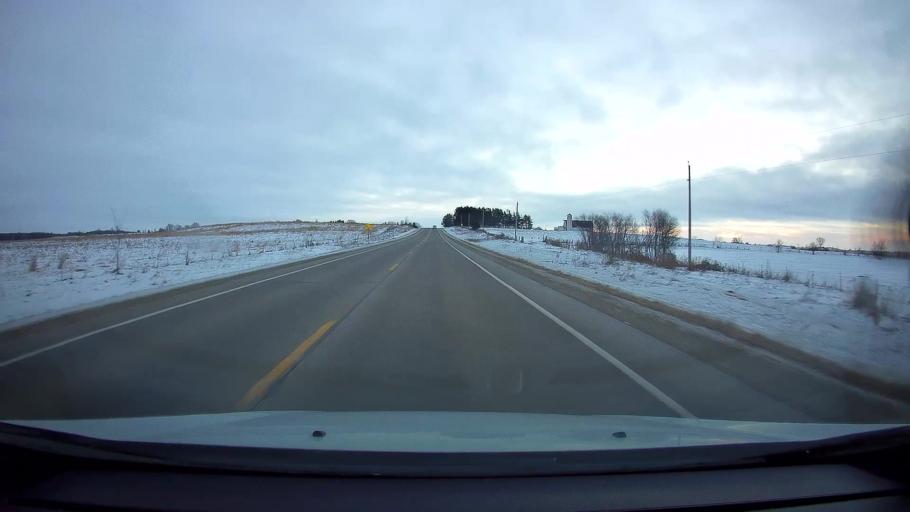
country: US
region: Wisconsin
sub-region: Saint Croix County
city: New Richmond
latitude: 45.1371
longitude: -92.5168
